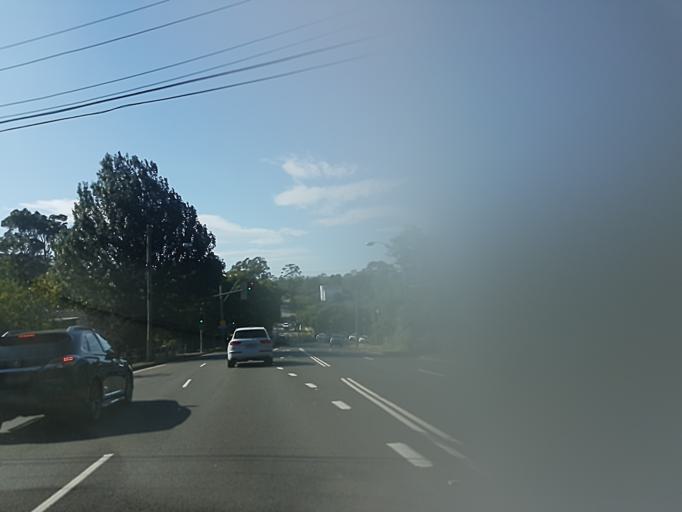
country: AU
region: New South Wales
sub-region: Willoughby
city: Castle Cove
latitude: -33.7925
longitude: 151.2073
